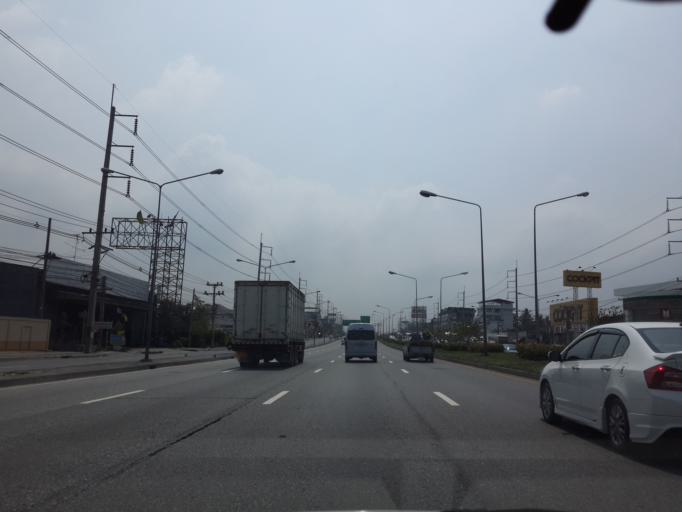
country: TH
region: Chon Buri
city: Chon Buri
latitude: 13.3946
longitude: 101.0098
